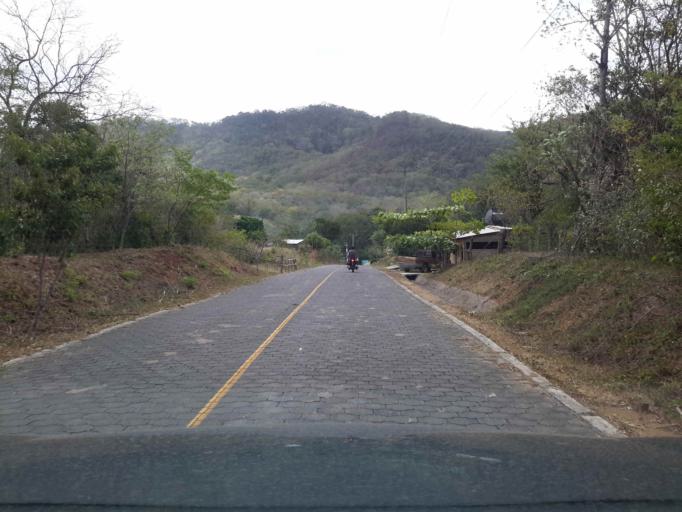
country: NI
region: Rivas
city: San Juan del Sur
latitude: 11.2296
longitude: -85.8254
